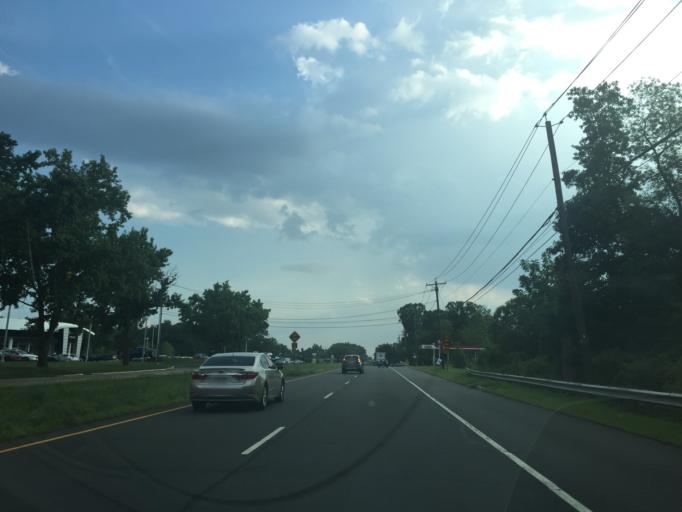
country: US
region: New Jersey
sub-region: Middlesex County
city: Cranbury
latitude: 40.2951
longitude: -74.5177
